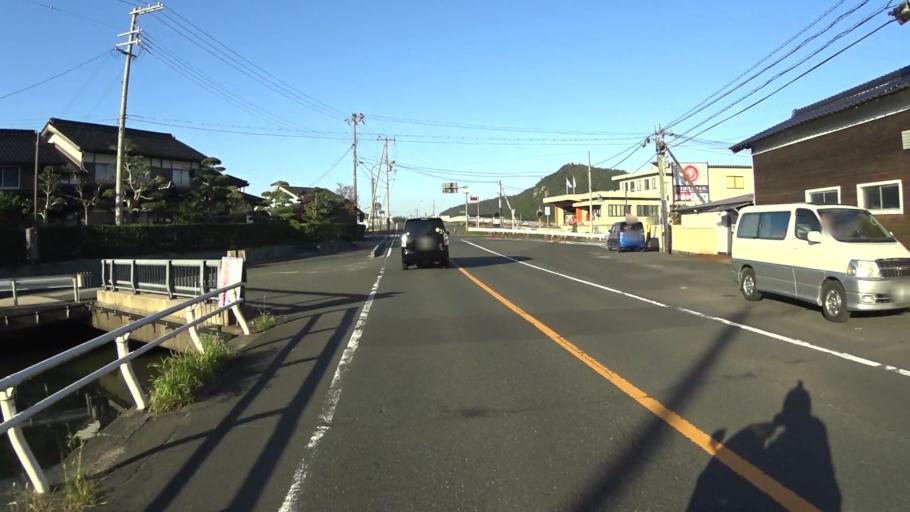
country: JP
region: Hyogo
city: Toyooka
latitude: 35.6073
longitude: 134.9183
